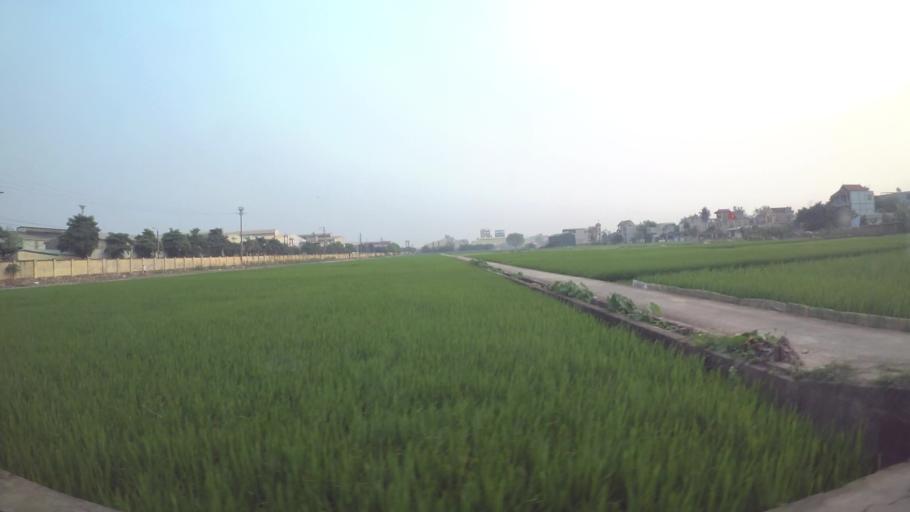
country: VN
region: Ha Noi
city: Thuong Tin
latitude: 20.8777
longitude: 105.8702
